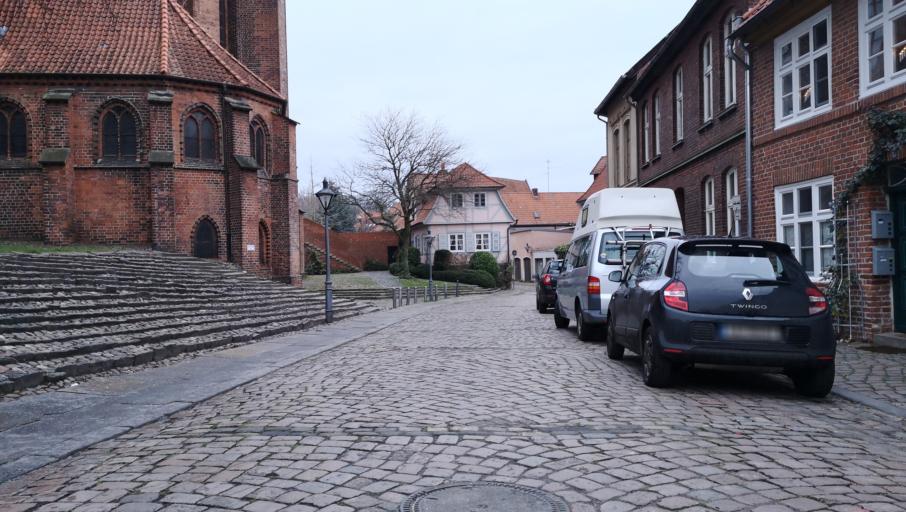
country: DE
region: Lower Saxony
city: Lueneburg
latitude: 53.2489
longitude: 10.4015
